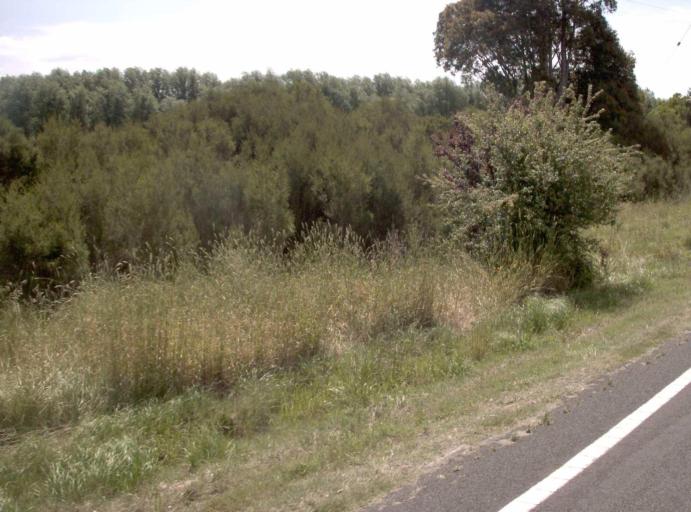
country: AU
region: Victoria
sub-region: Wellington
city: Sale
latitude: -38.0531
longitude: 147.0671
